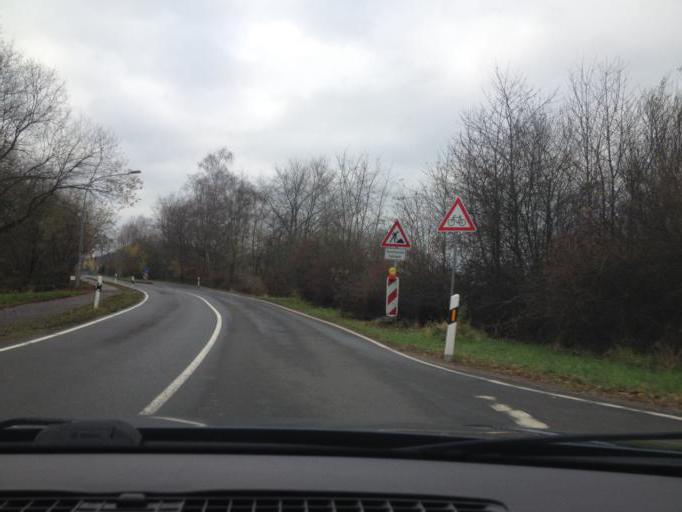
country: DE
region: Saarland
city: Ottweiler
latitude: 49.3713
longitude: 7.1665
